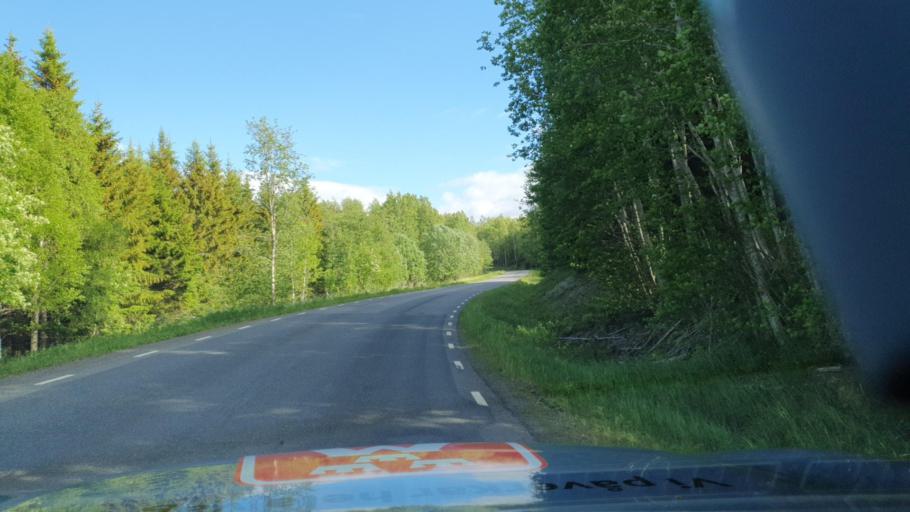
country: SE
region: Vaesternorrland
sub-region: Kramfors Kommun
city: Nordingra
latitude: 62.8109
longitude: 18.1409
